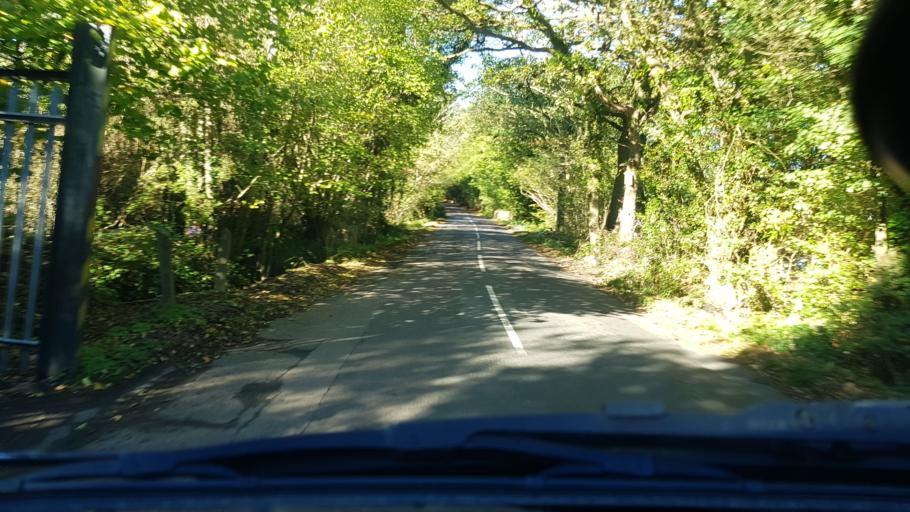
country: GB
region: England
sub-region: Surrey
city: Pirbright
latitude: 51.2662
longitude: -0.6441
